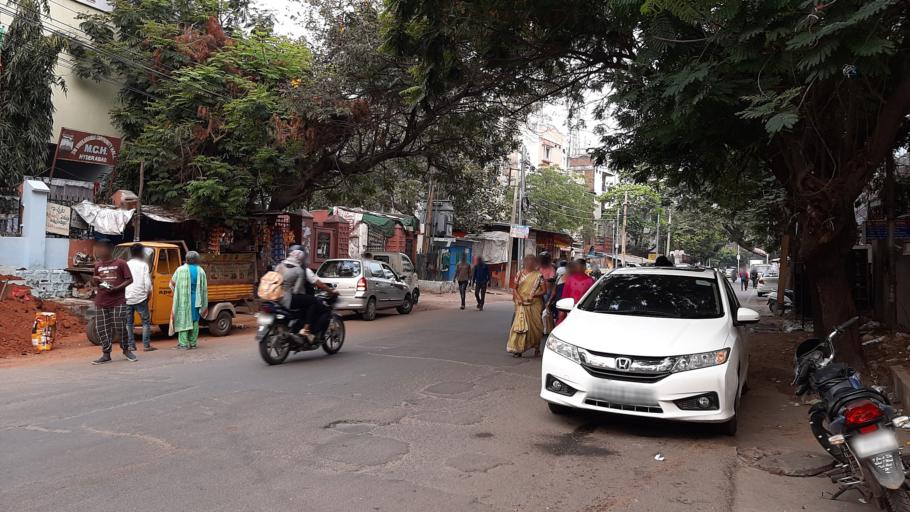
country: IN
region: Telangana
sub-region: Hyderabad
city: Hyderabad
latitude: 17.4387
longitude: 78.4492
